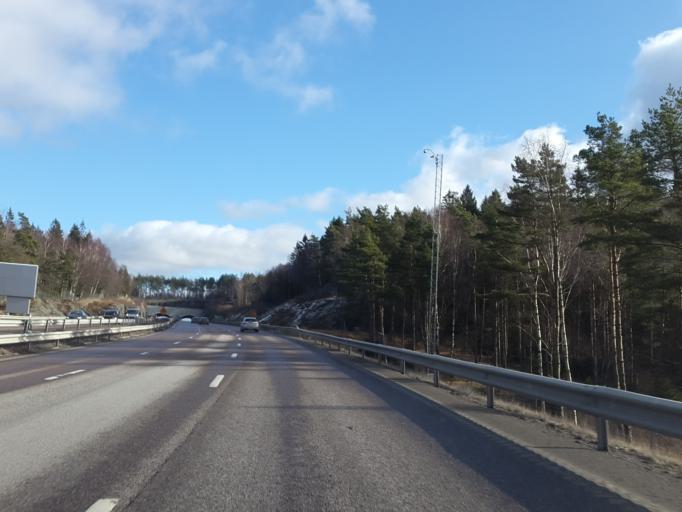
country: SE
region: Vaestra Goetaland
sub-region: Partille Kommun
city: Furulund
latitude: 57.7402
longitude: 12.1765
